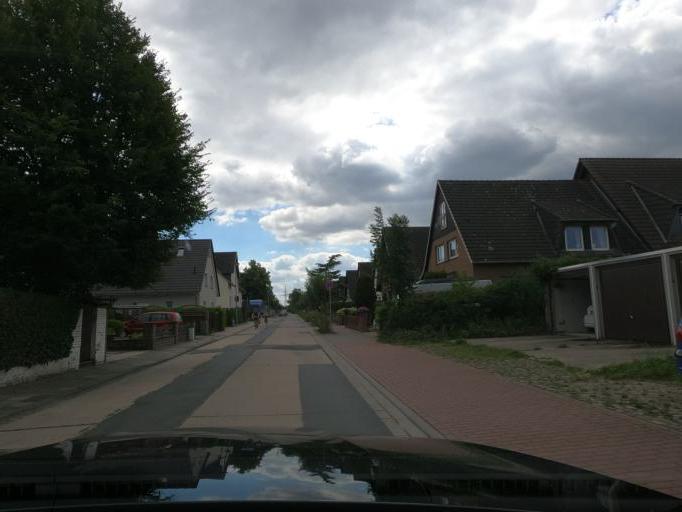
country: DE
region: Lower Saxony
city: Sehnde
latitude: 52.3499
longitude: 9.8897
